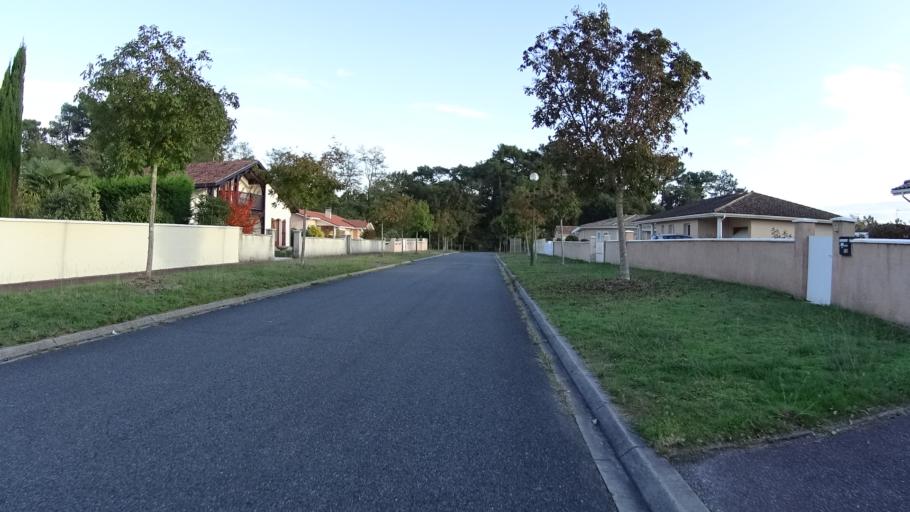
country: FR
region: Aquitaine
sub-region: Departement des Landes
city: Saint-Paul-les-Dax
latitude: 43.7352
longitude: -1.0452
